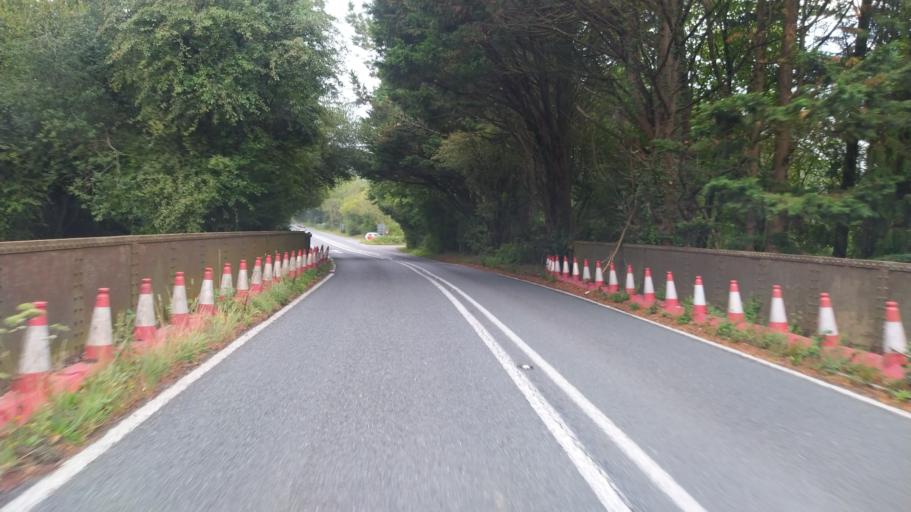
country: GB
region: England
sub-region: Hampshire
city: New Milton
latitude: 50.8050
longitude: -1.6715
